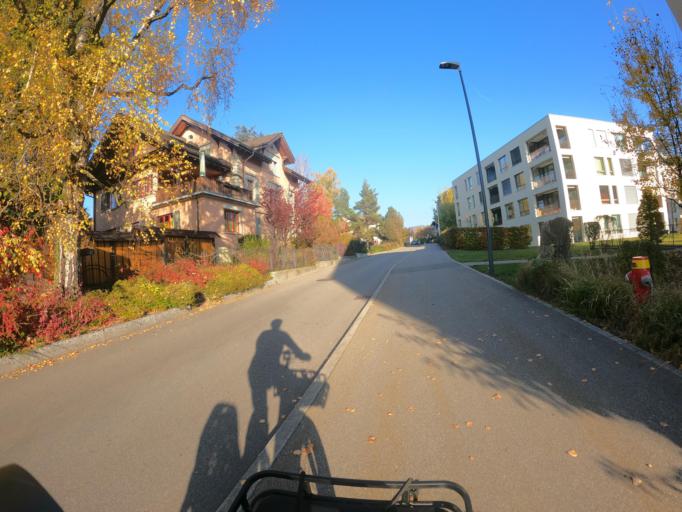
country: CH
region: Zurich
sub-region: Bezirk Affoltern
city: Affoltern / Oberdorf
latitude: 47.2751
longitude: 8.4424
